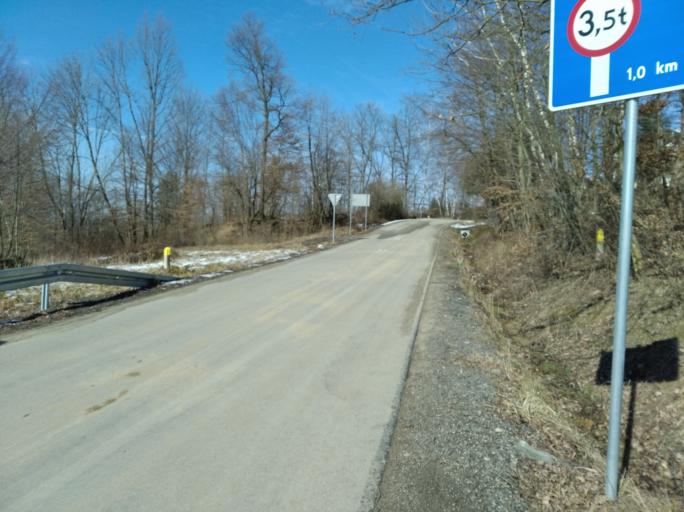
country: PL
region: Subcarpathian Voivodeship
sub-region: Powiat brzozowski
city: Jablonica Polska
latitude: 49.7167
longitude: 21.8803
